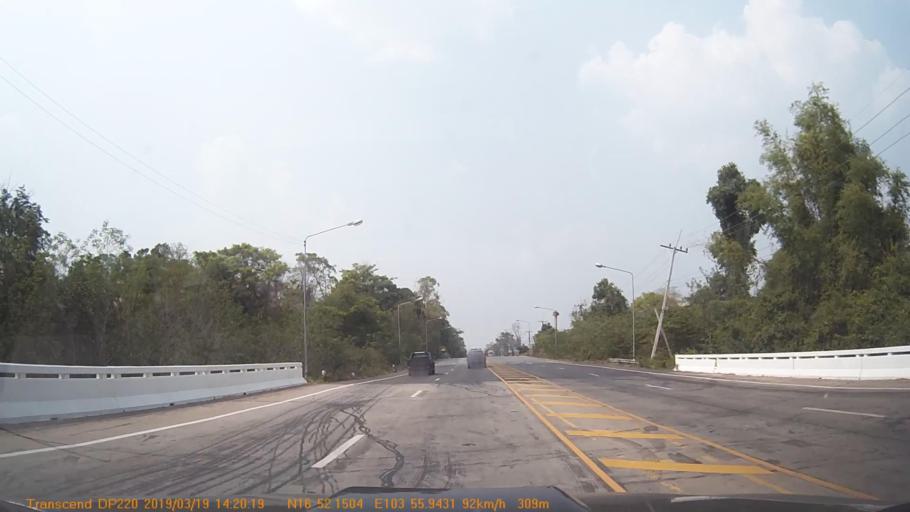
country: TH
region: Sakon Nakhon
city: Phu Phan
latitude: 16.8697
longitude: 103.9323
